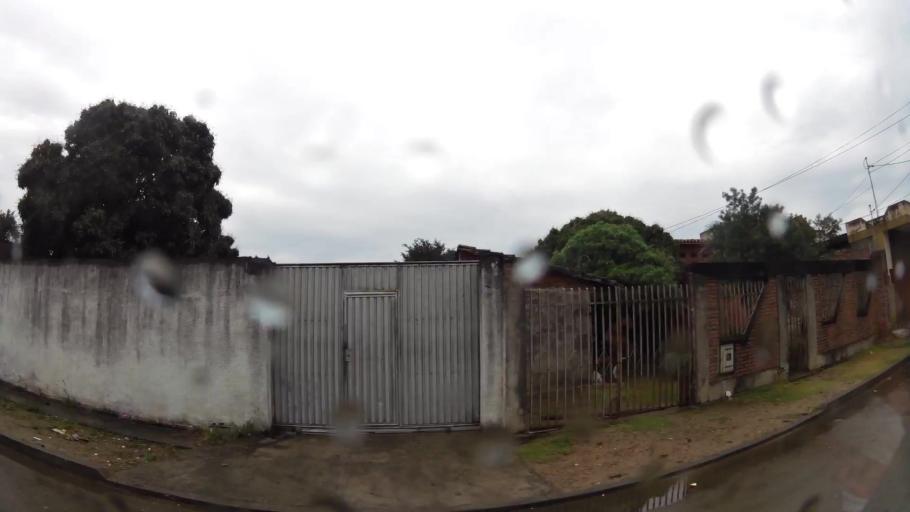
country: BO
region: Santa Cruz
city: Santa Cruz de la Sierra
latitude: -17.8144
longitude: -63.2038
